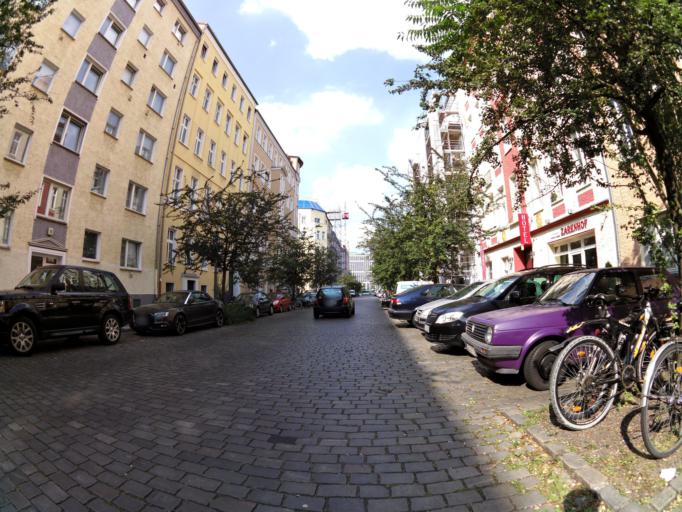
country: DE
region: Berlin
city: Mitte
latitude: 52.5298
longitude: 13.3878
